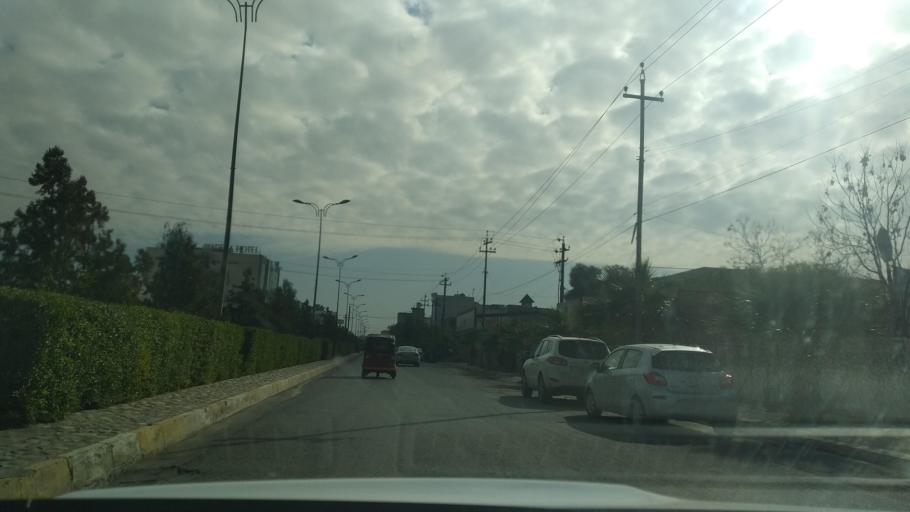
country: IQ
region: Arbil
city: Erbil
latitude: 36.1797
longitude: 44.0263
